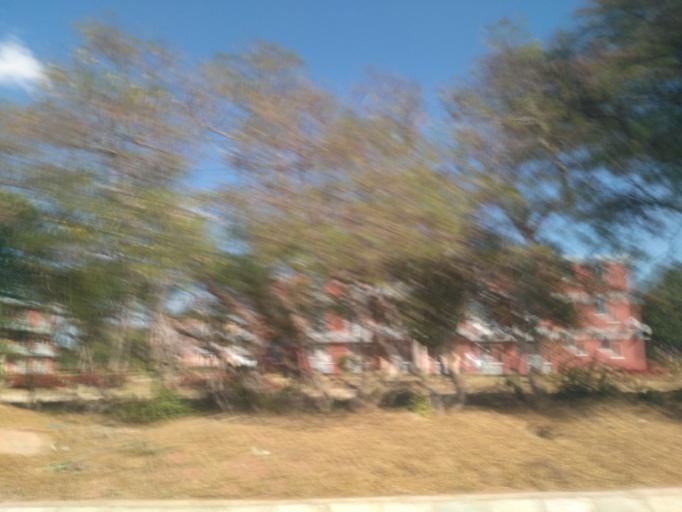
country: TZ
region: Dodoma
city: Dodoma
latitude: -6.1921
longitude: 35.7370
